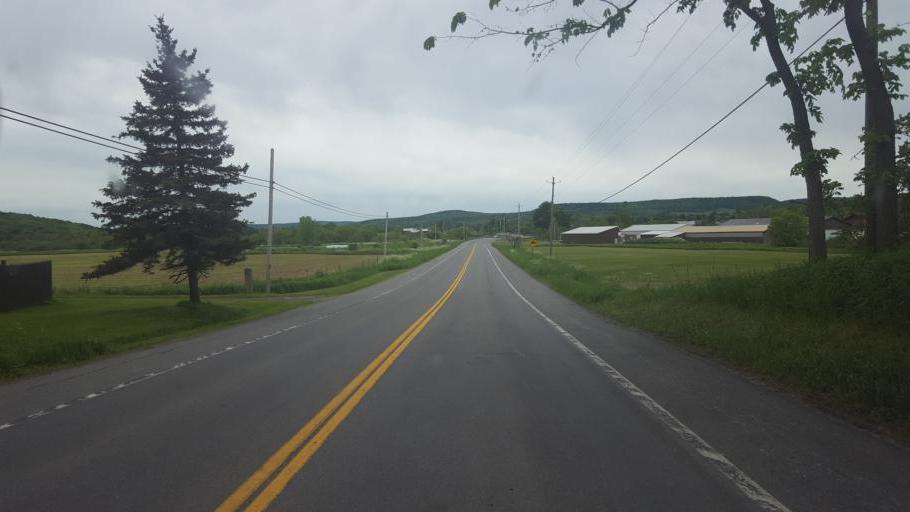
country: US
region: New York
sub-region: Otsego County
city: Richfield Springs
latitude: 42.8888
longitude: -75.1517
